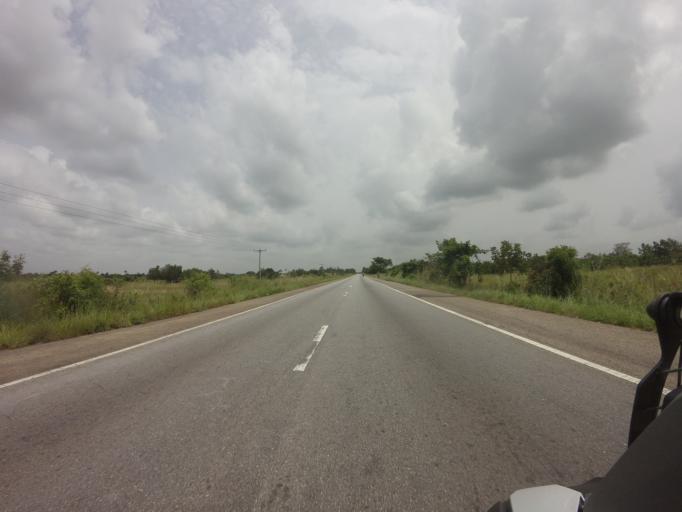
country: GH
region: Volta
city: Keta
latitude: 6.0675
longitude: 0.7367
